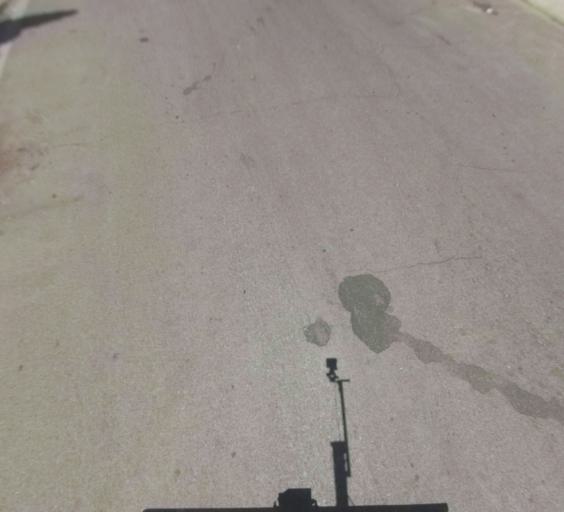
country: US
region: California
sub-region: Madera County
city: Parksdale
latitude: 36.9461
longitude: -120.0349
